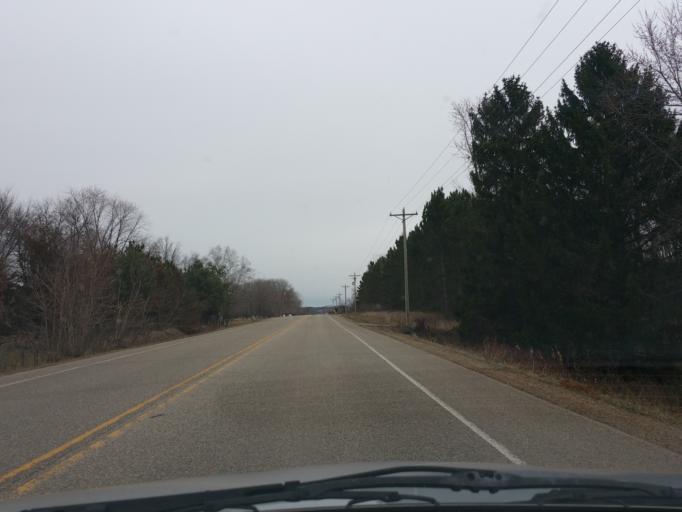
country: US
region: Wisconsin
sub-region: Saint Croix County
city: North Hudson
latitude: 45.0033
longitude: -92.6647
